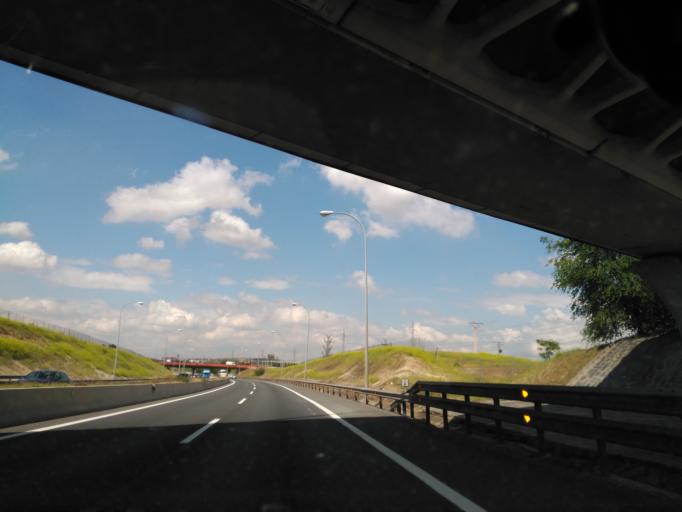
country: ES
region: Madrid
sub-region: Provincia de Madrid
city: Villaverde
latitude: 40.3361
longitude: -3.6758
